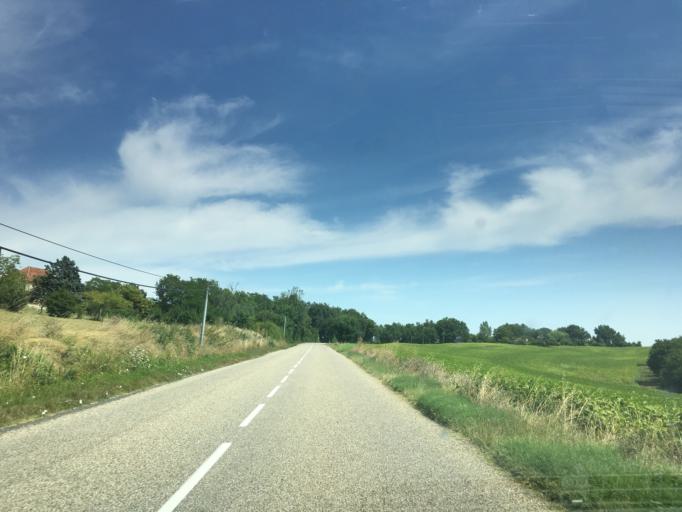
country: FR
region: Midi-Pyrenees
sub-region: Departement du Gers
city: Fleurance
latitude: 43.8655
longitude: 0.7066
